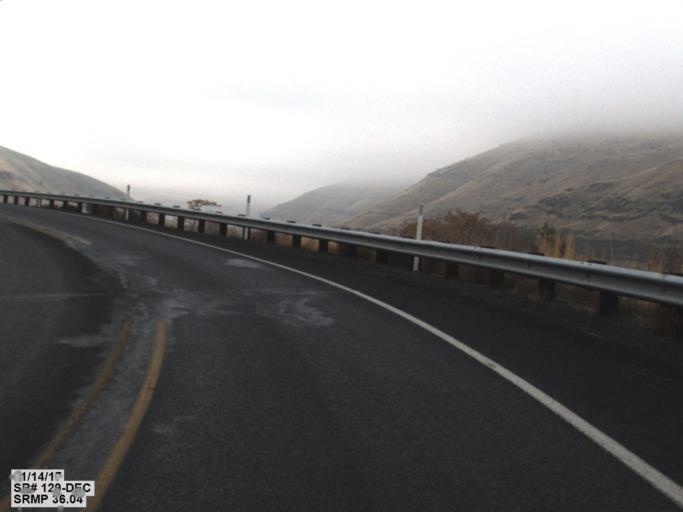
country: US
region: Washington
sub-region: Asotin County
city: Asotin
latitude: 46.3389
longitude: -117.0516
